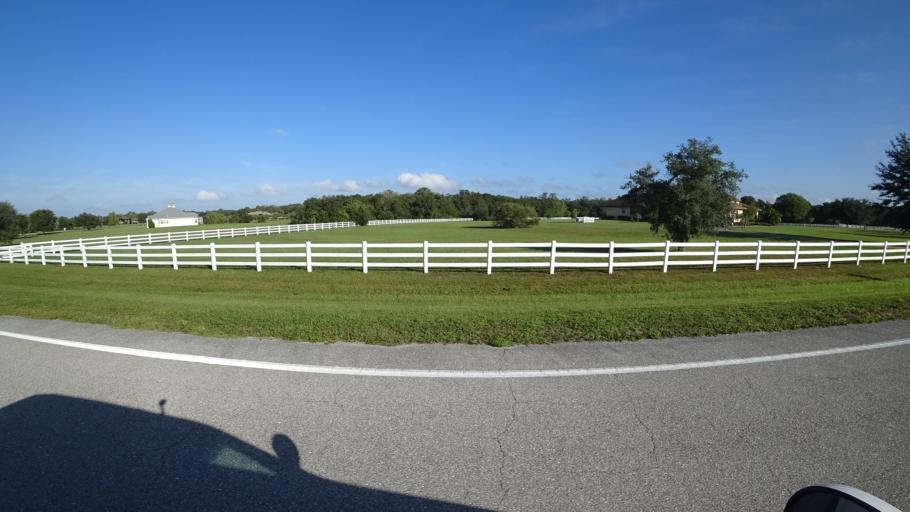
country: US
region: Florida
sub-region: Hillsborough County
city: Sun City Center
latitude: 27.5576
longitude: -82.3550
